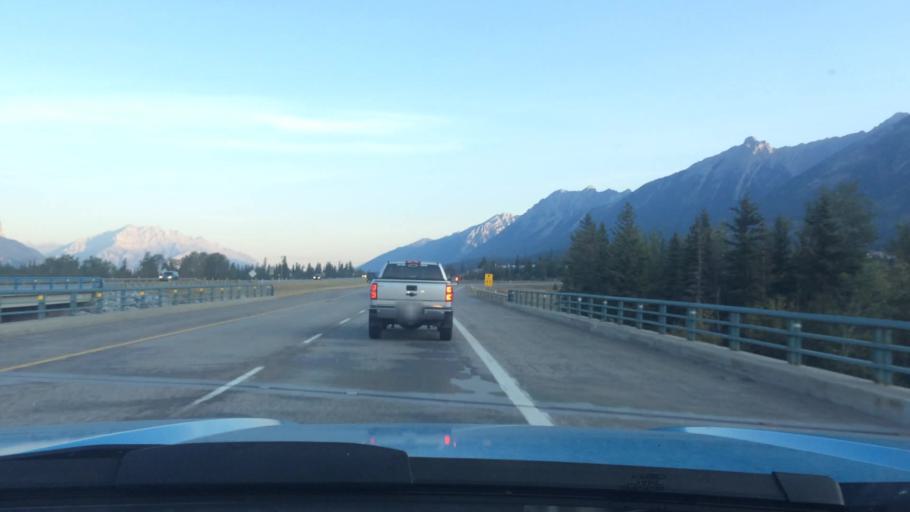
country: CA
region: Alberta
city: Canmore
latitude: 51.0751
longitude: -115.3305
